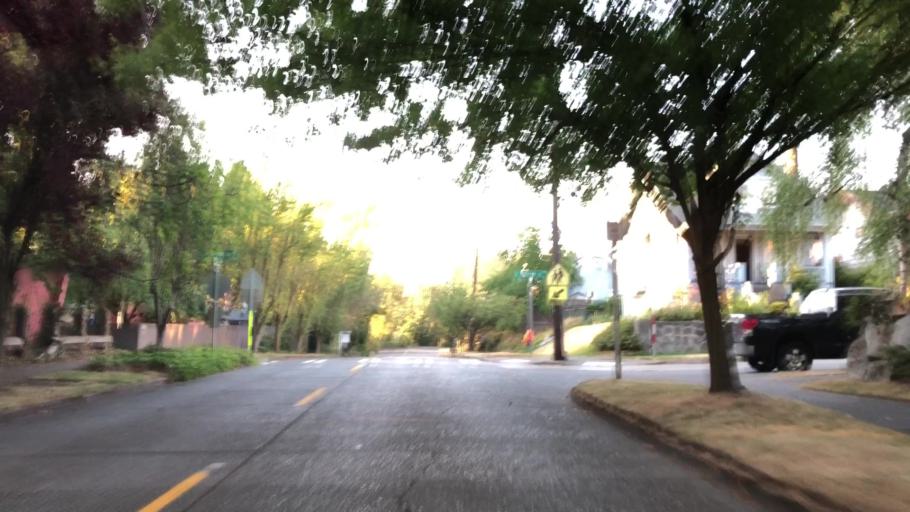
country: US
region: Washington
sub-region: King County
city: Seattle
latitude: 47.6400
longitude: -122.3072
